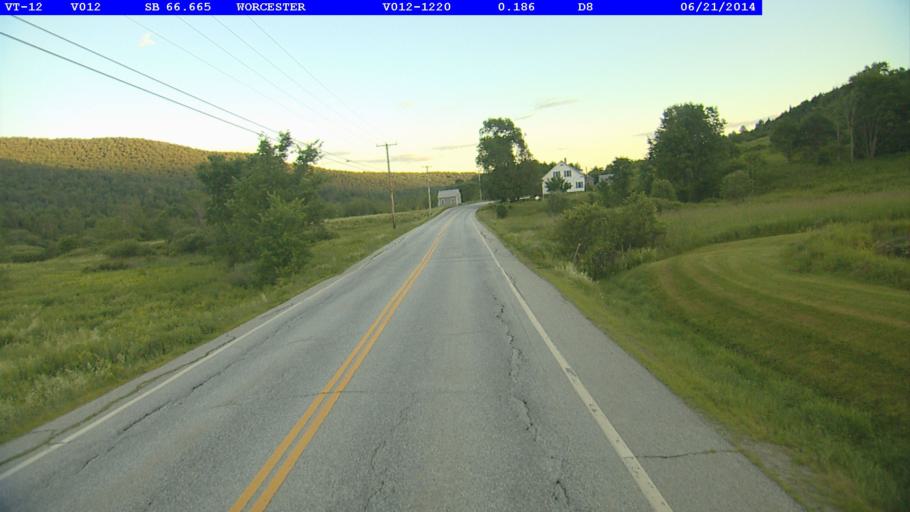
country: US
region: Vermont
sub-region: Washington County
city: Montpelier
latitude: 44.3553
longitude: -72.5648
